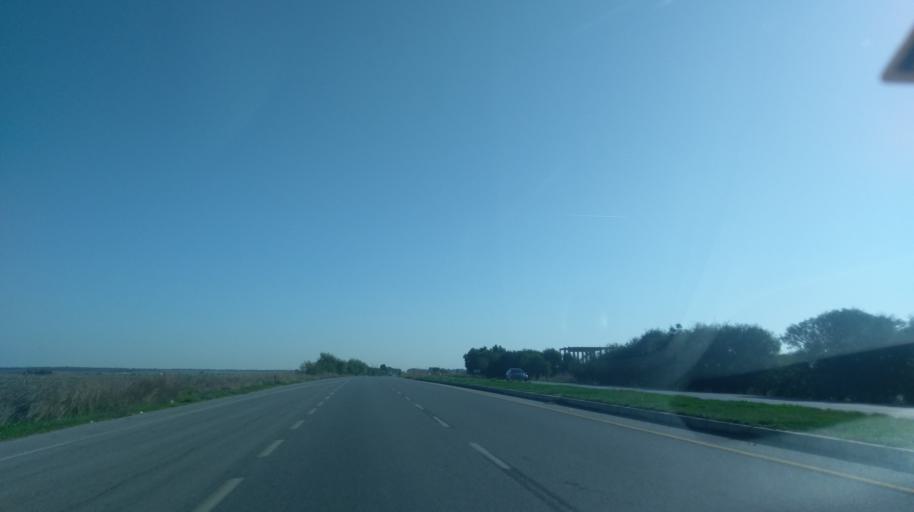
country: CY
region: Larnaka
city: Athienou
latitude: 35.2109
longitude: 33.5590
